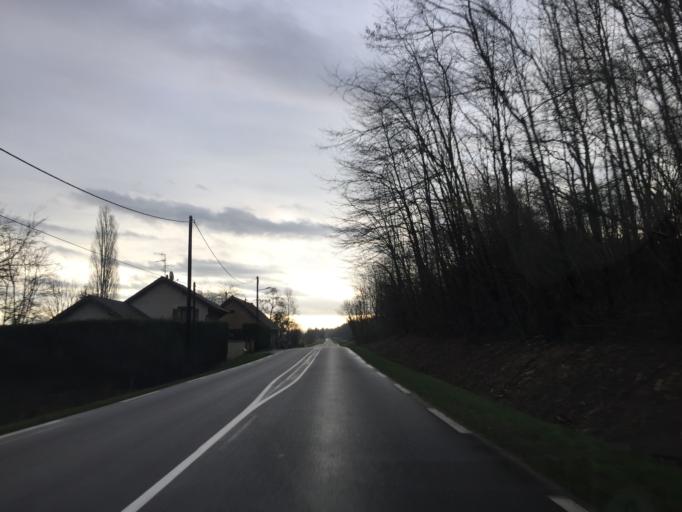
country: FR
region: Franche-Comte
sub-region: Departement du Jura
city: Mont-sous-Vaudrey
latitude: 47.0014
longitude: 5.5289
